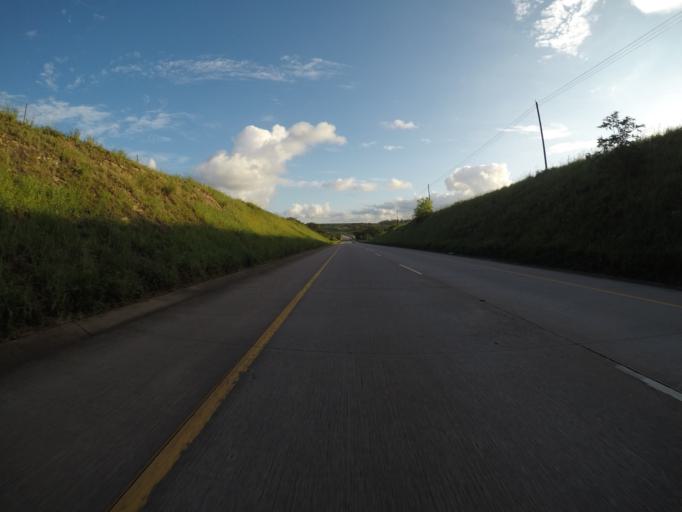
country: ZA
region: KwaZulu-Natal
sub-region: uMkhanyakude District Municipality
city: Mtubatuba
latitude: -28.4999
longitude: 32.1385
